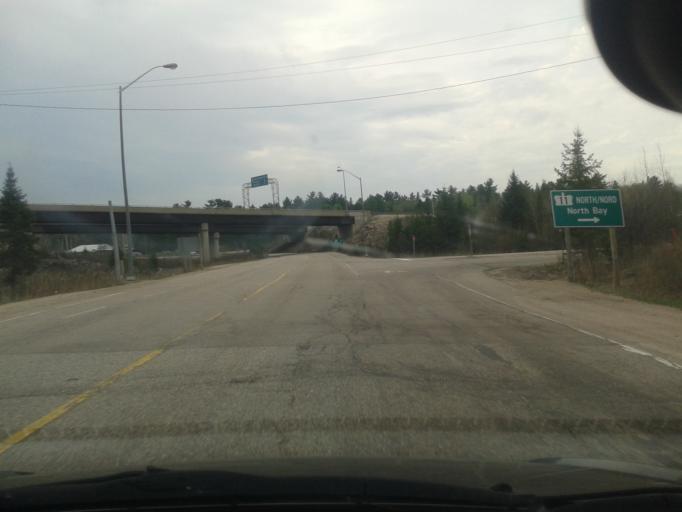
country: CA
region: Ontario
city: Powassan
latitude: 46.1952
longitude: -79.3541
